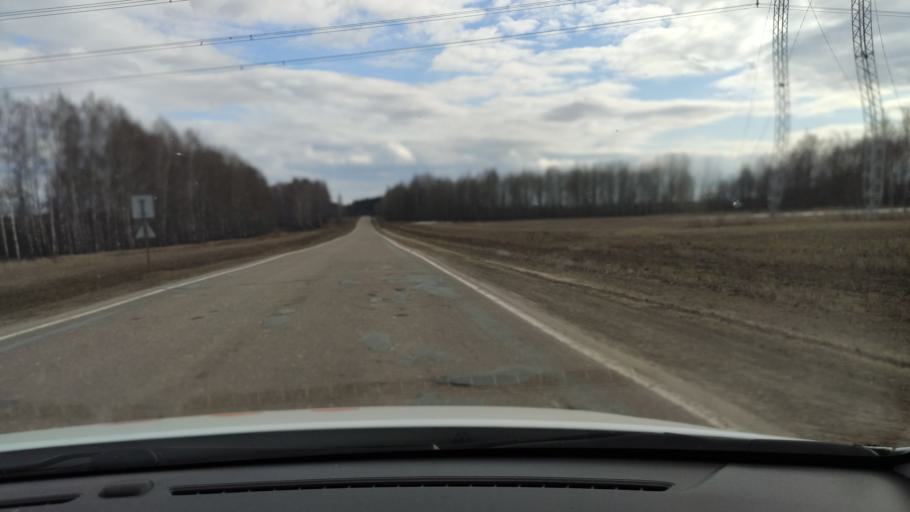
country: RU
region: Tatarstan
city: Vysokaya Gora
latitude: 56.0734
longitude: 49.1910
